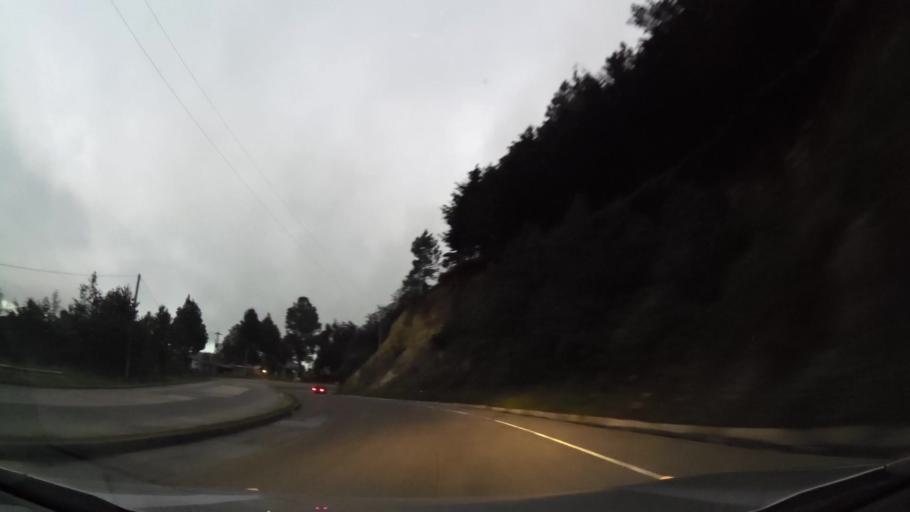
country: GT
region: Chimaltenango
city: Santa Apolonia
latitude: 14.8245
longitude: -91.0081
